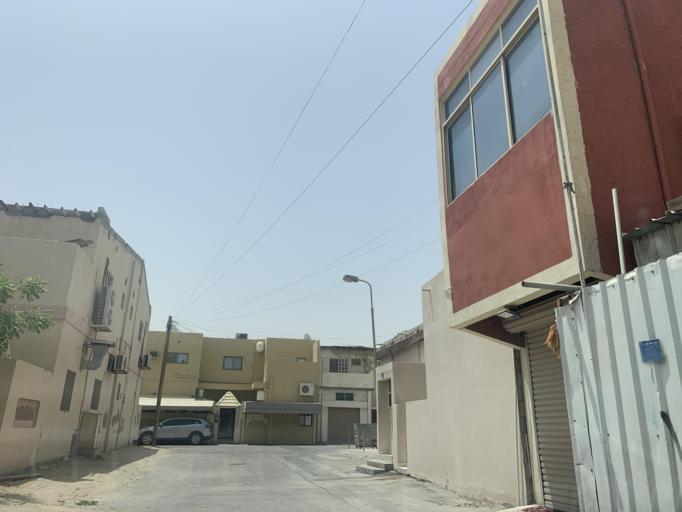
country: BH
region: Northern
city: Madinat `Isa
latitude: 26.1528
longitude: 50.5195
